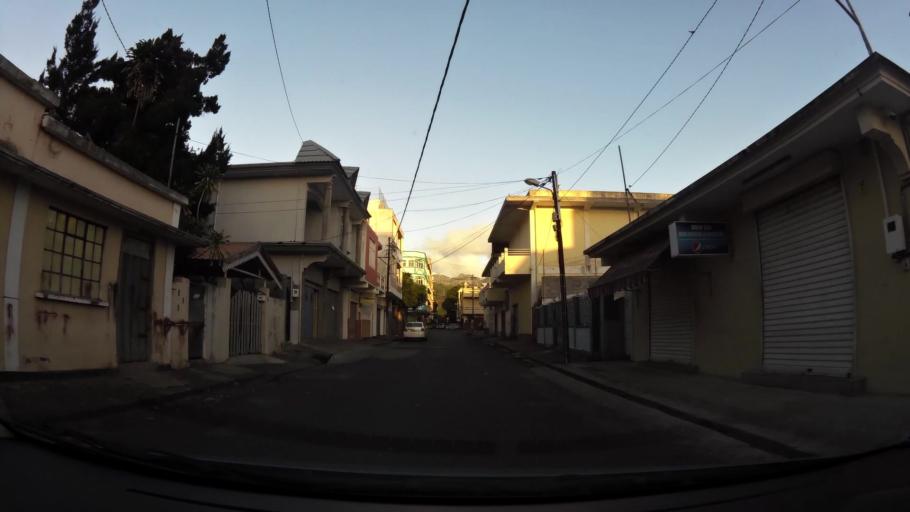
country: MU
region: Port Louis
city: Port Louis
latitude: -20.1540
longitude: 57.5104
